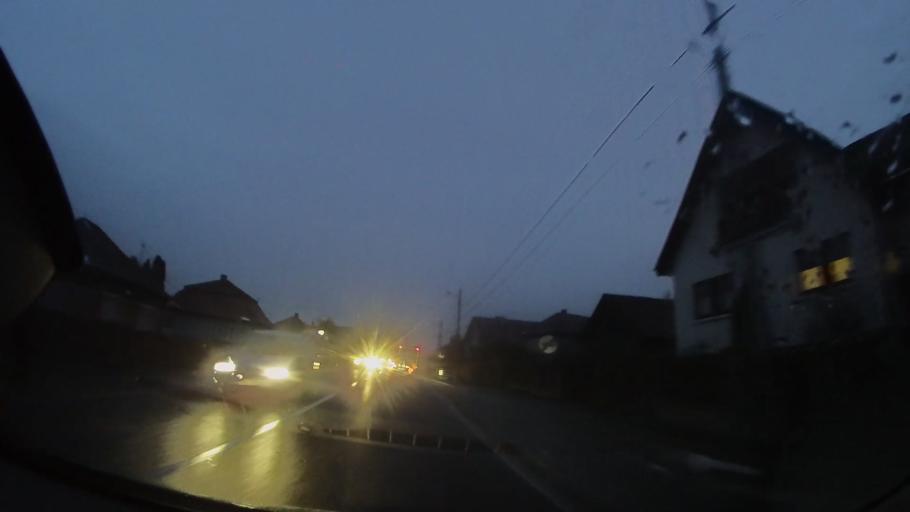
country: RO
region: Harghita
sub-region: Comuna Ditrau
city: Ditrau
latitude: 46.8106
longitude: 25.4939
